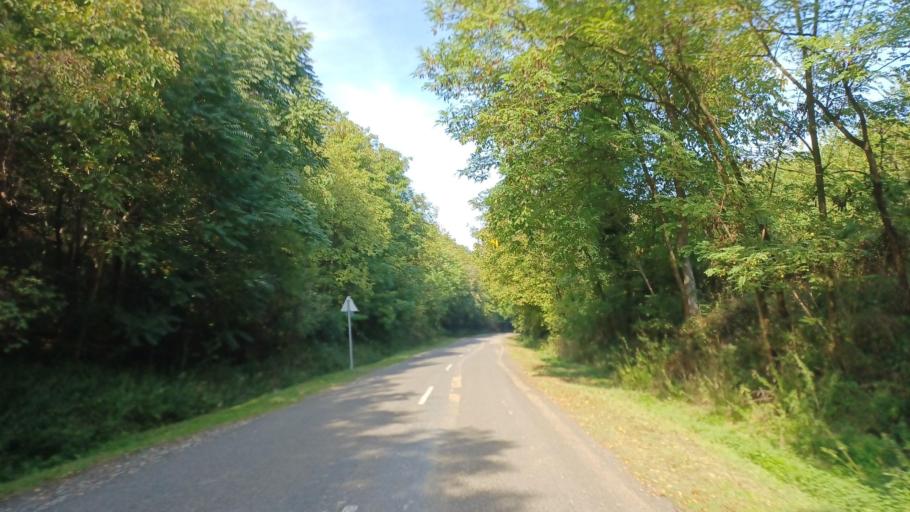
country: HU
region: Tolna
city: Pincehely
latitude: 46.6768
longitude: 18.4671
